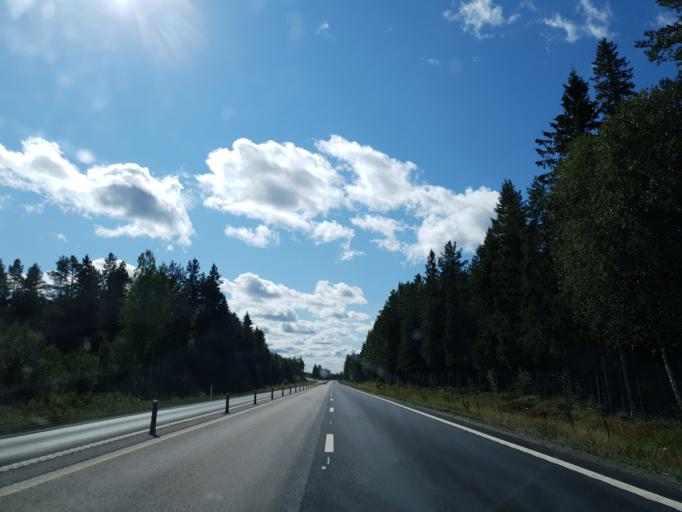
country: SE
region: Vaesterbotten
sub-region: Nordmalings Kommun
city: Nordmaling
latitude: 63.5435
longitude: 19.4083
